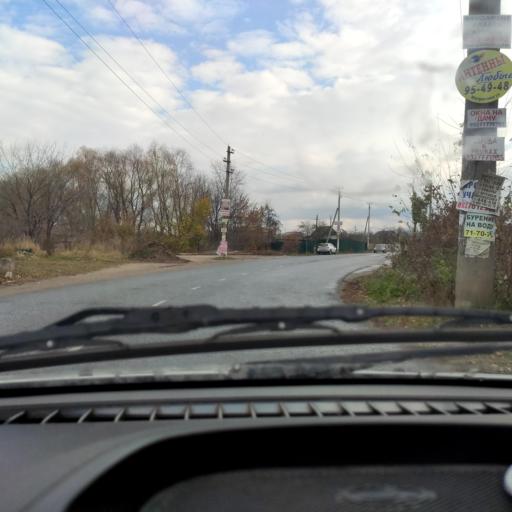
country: RU
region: Samara
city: Zhigulevsk
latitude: 53.4664
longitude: 49.6390
